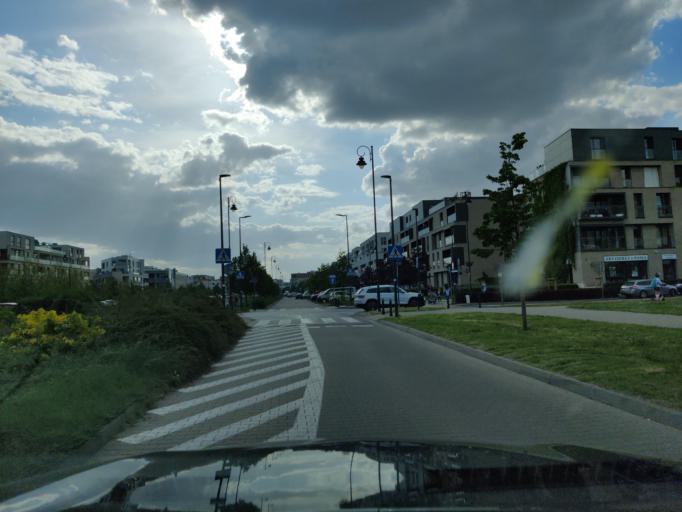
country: PL
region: Masovian Voivodeship
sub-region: Warszawa
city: Wilanow
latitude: 52.1650
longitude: 21.0751
